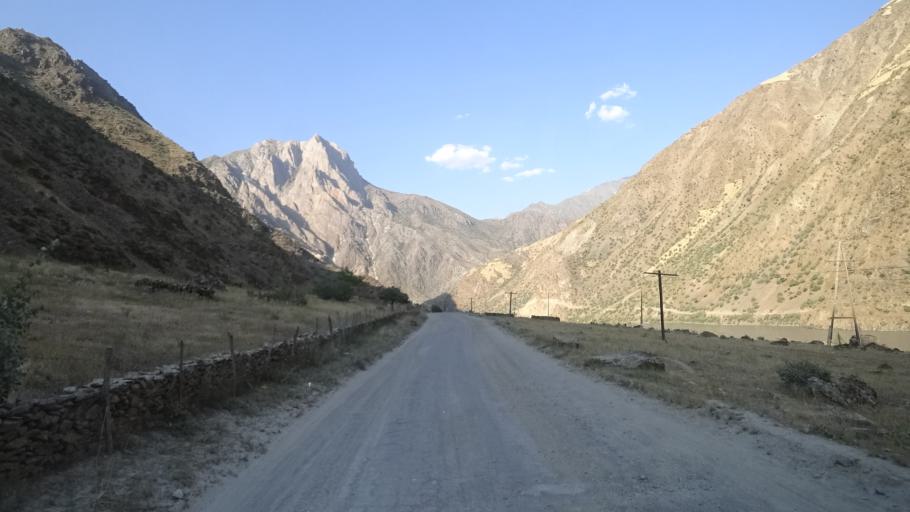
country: AF
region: Badakhshan
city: Maymay
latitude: 38.4778
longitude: 70.9699
